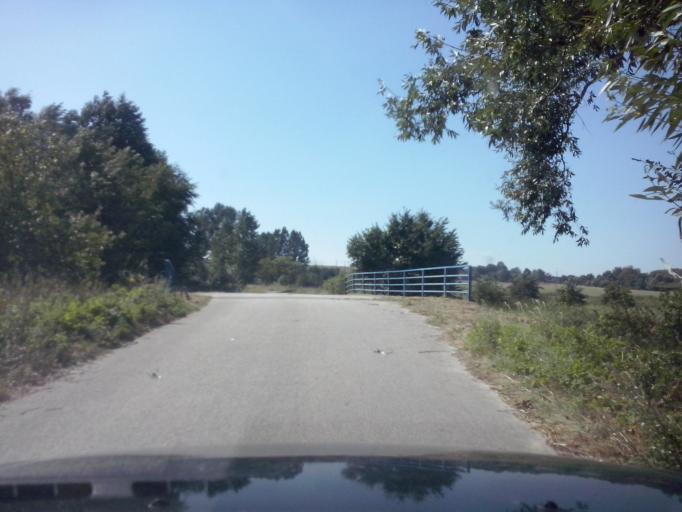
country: PL
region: Swietokrzyskie
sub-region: Powiat buski
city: Gnojno
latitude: 50.6043
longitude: 20.8027
